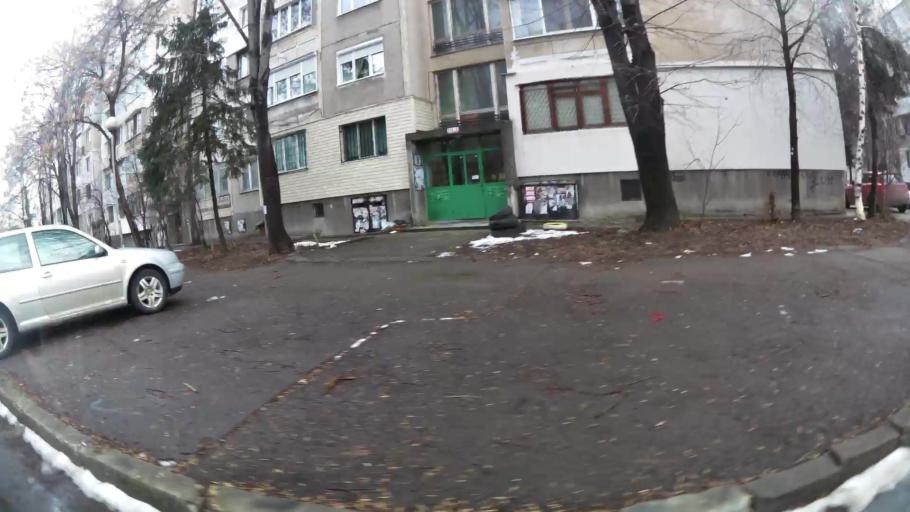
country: BG
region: Sofiya
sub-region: Obshtina Bozhurishte
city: Bozhurishte
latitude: 42.7190
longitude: 23.2401
